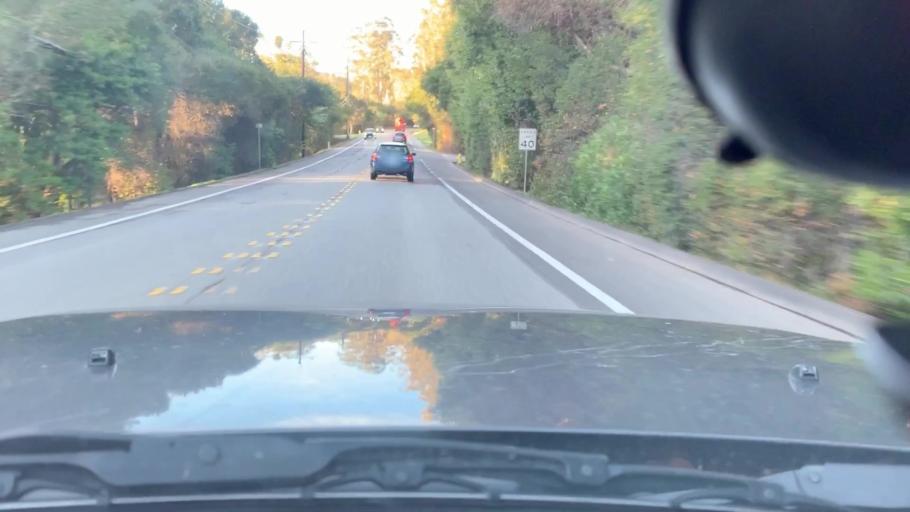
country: US
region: California
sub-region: San Mateo County
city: Woodside
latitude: 37.4111
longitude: -122.2414
